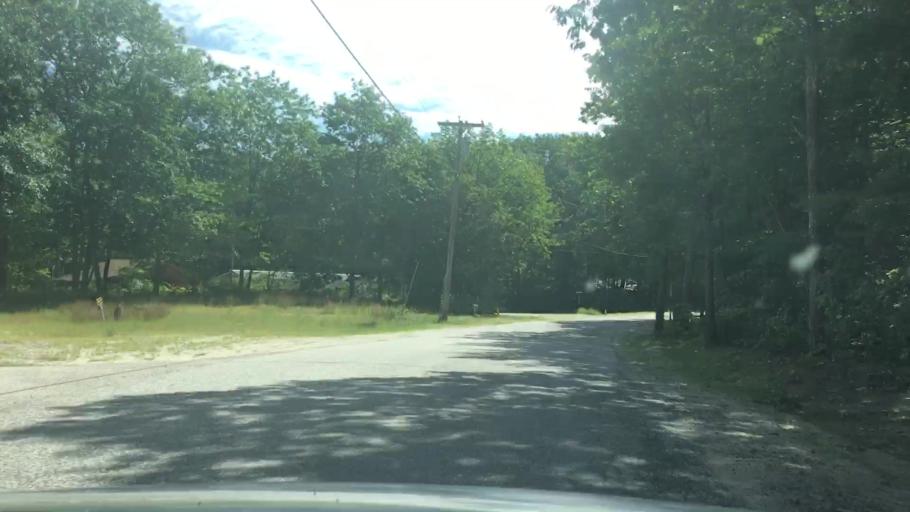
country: US
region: Maine
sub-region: Androscoggin County
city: Turner
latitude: 44.1919
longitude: -70.2440
